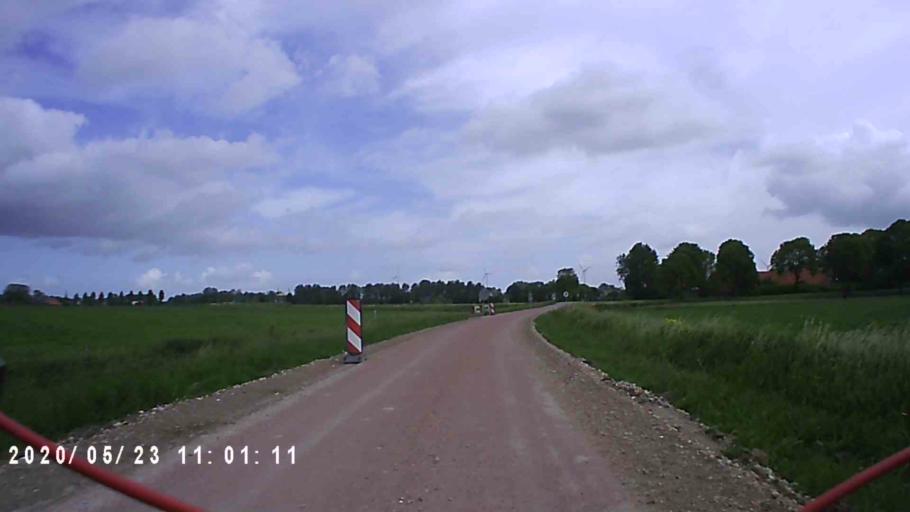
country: NL
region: Groningen
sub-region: Gemeente Delfzijl
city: Delfzijl
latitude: 53.3083
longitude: 6.9436
